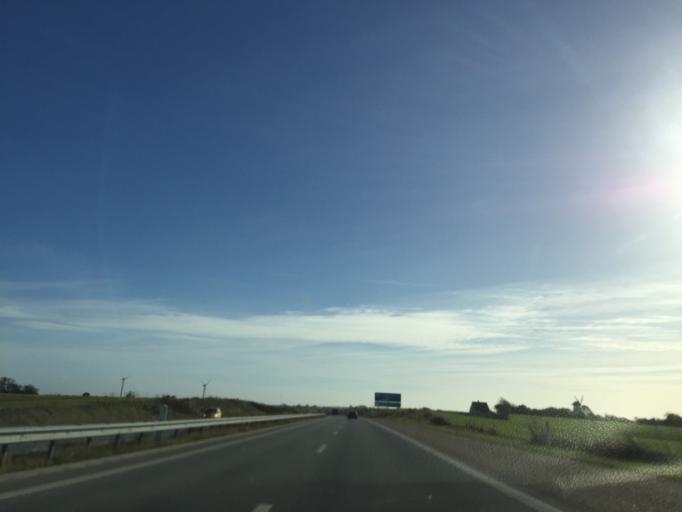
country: DK
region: South Denmark
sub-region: Sonderborg Kommune
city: Broager
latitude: 54.9407
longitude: 9.6636
